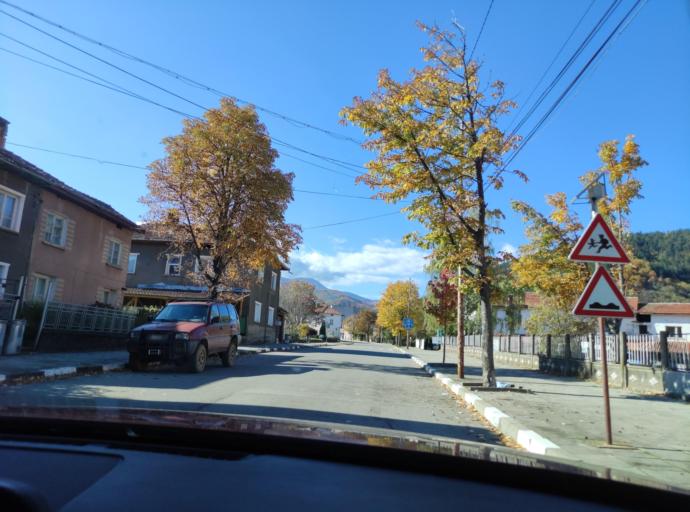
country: BG
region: Montana
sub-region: Obshtina Chiprovtsi
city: Chiprovtsi
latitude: 43.3844
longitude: 22.8858
